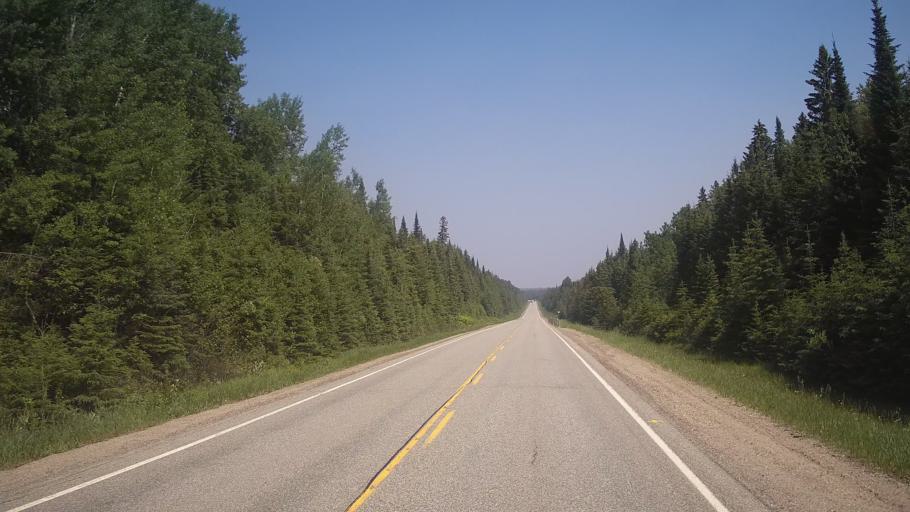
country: CA
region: Ontario
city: Timmins
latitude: 48.2031
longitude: -81.5782
